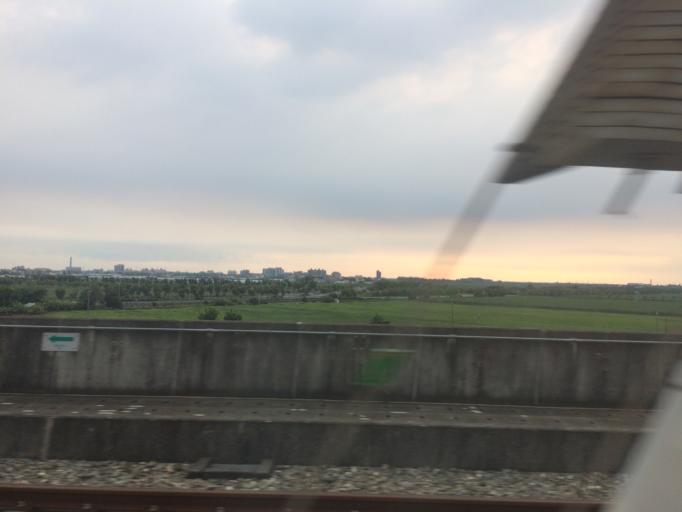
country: TW
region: Taiwan
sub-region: Chiayi
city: Taibao
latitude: 23.4655
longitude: 120.3241
